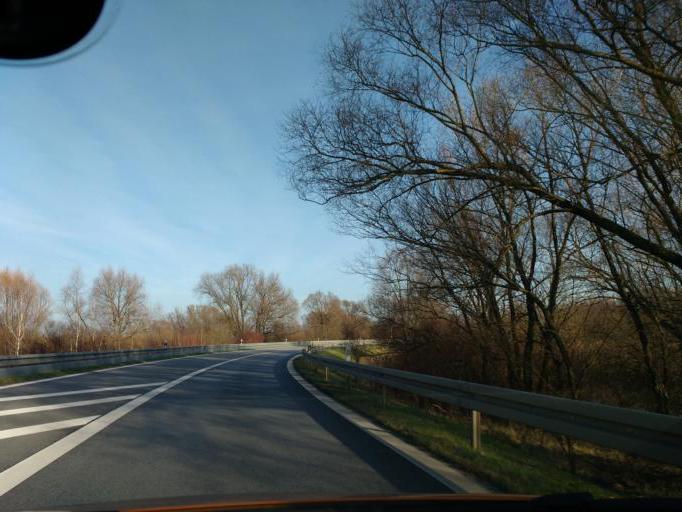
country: DE
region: Berlin
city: Buchholz
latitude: 52.6388
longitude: 13.4275
